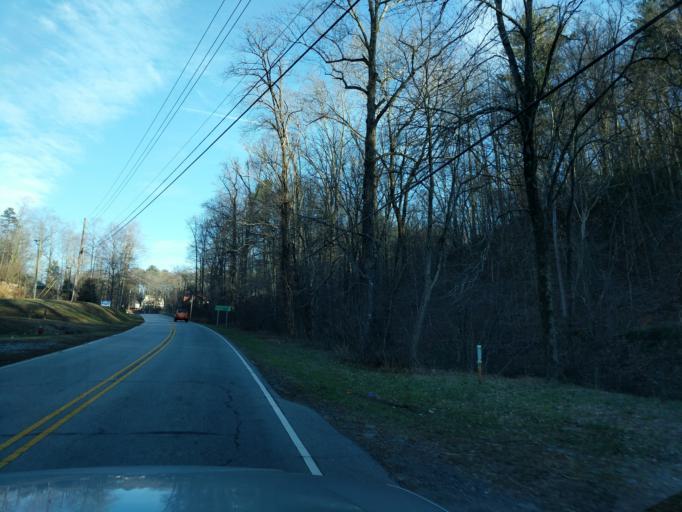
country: US
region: North Carolina
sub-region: Rutherford County
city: Lake Lure
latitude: 35.4303
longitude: -82.2237
